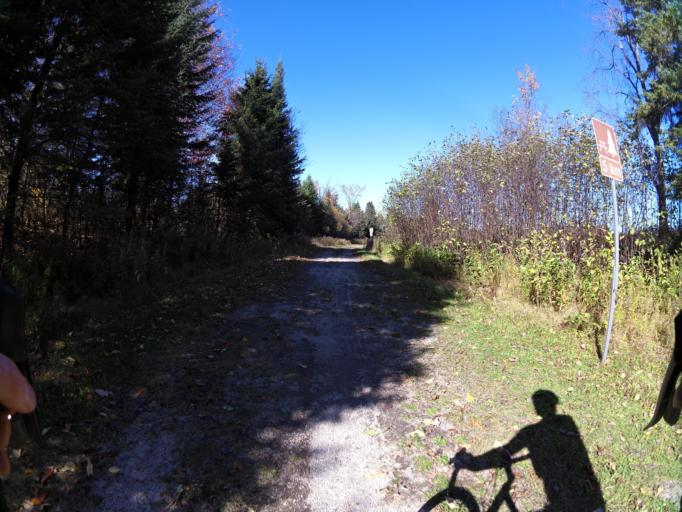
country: CA
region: Quebec
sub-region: Outaouais
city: Wakefield
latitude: 45.8726
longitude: -76.0265
